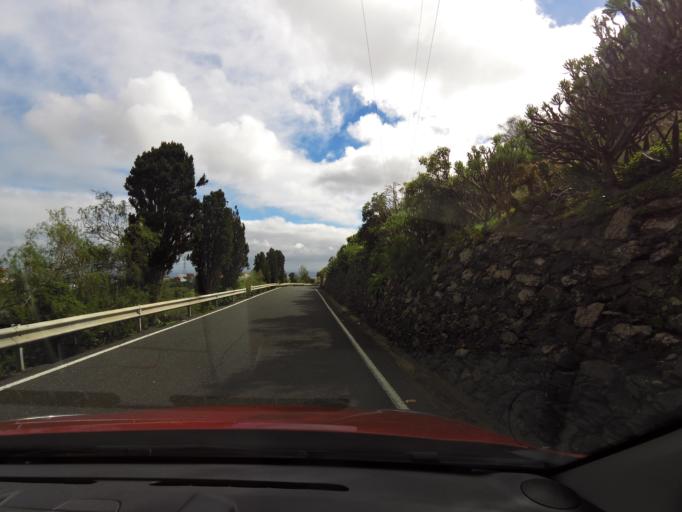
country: ES
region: Canary Islands
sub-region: Provincia de Las Palmas
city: Telde
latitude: 28.0179
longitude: -15.4531
